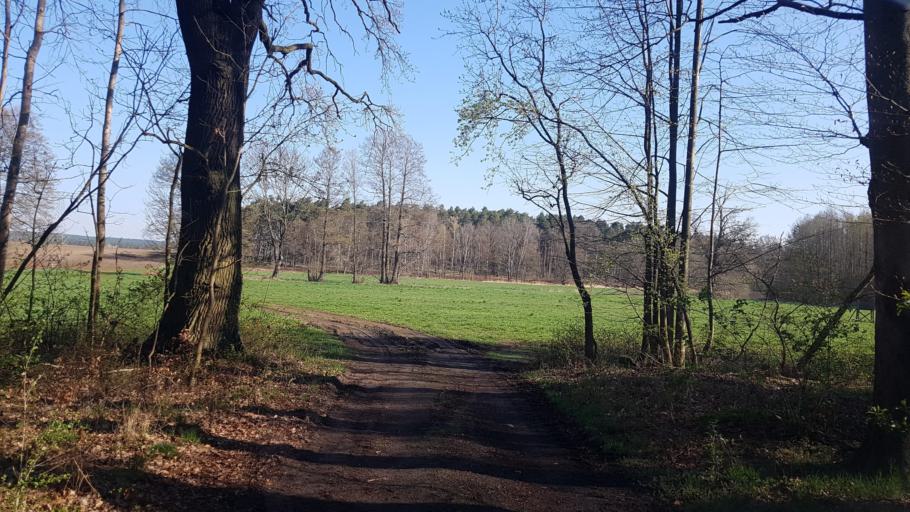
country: DE
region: Brandenburg
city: Altdobern
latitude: 51.6737
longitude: 13.9997
